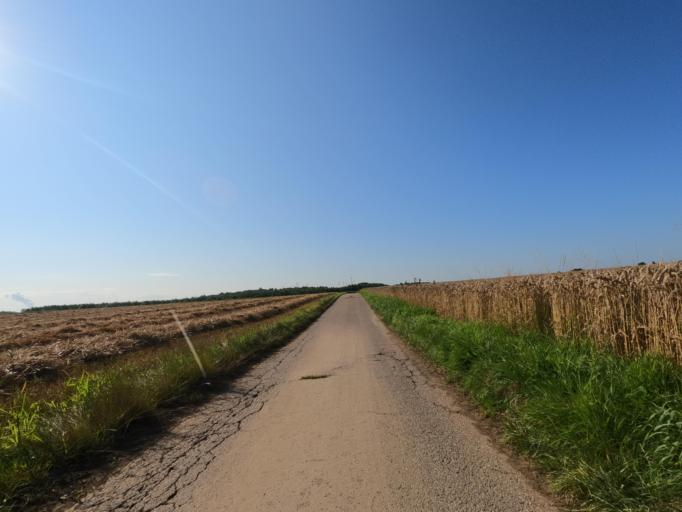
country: DE
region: North Rhine-Westphalia
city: Erkelenz
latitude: 51.0639
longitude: 6.3613
